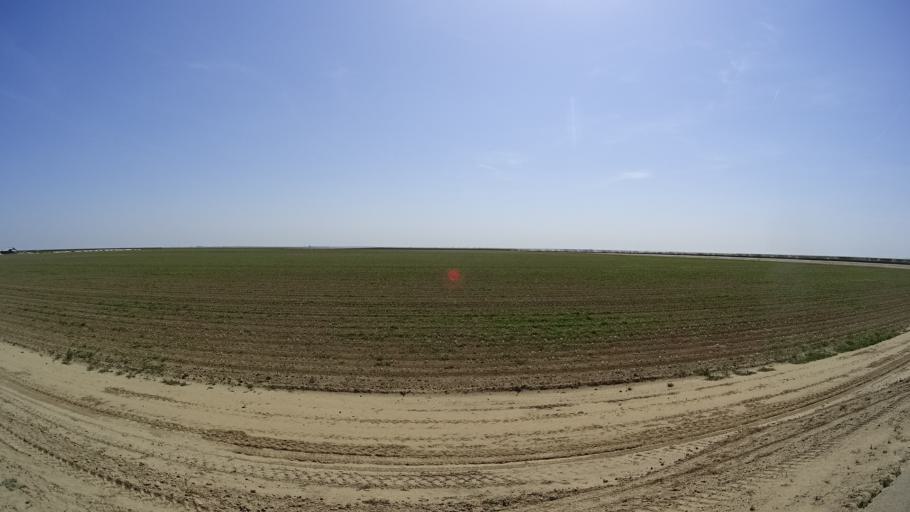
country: US
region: California
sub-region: Kings County
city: Kettleman City
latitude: 36.0699
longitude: -120.0037
